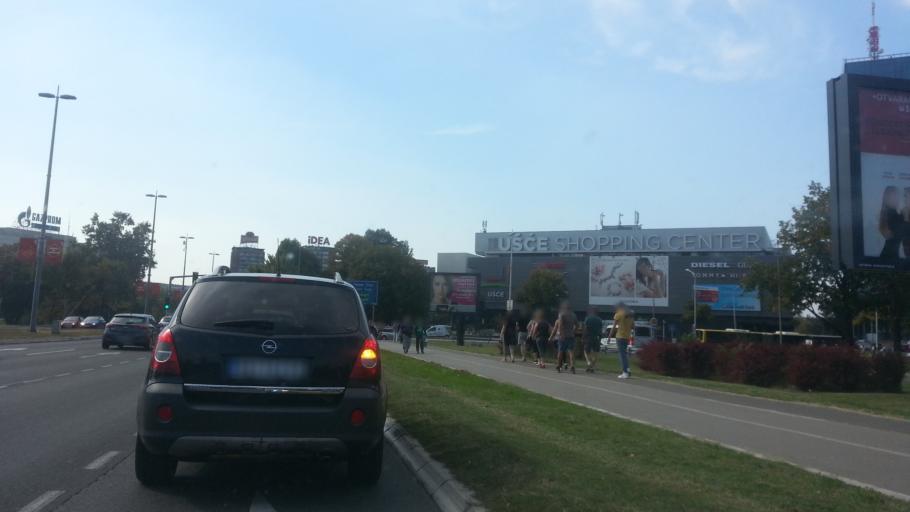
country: RS
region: Central Serbia
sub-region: Belgrade
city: Novi Beograd
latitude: 44.8146
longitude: 20.4404
